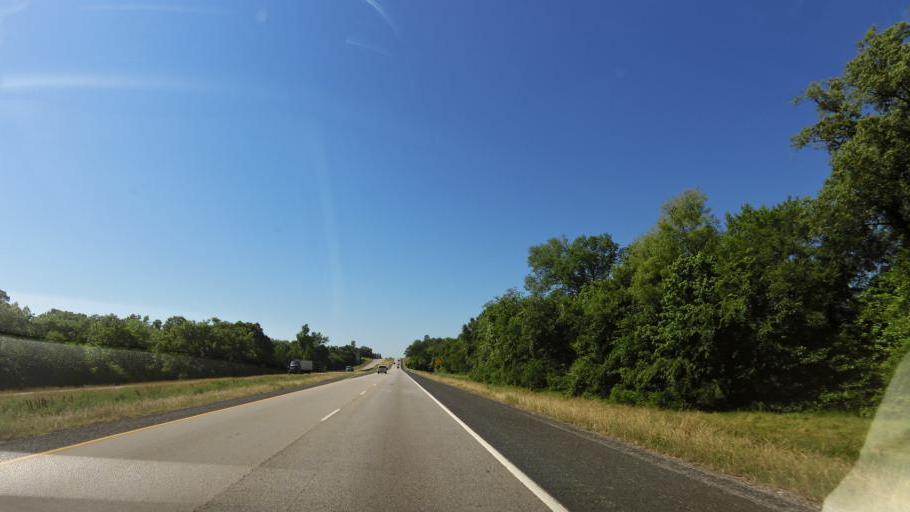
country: US
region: Texas
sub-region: Angelina County
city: Redland
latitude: 31.4509
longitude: -94.7267
